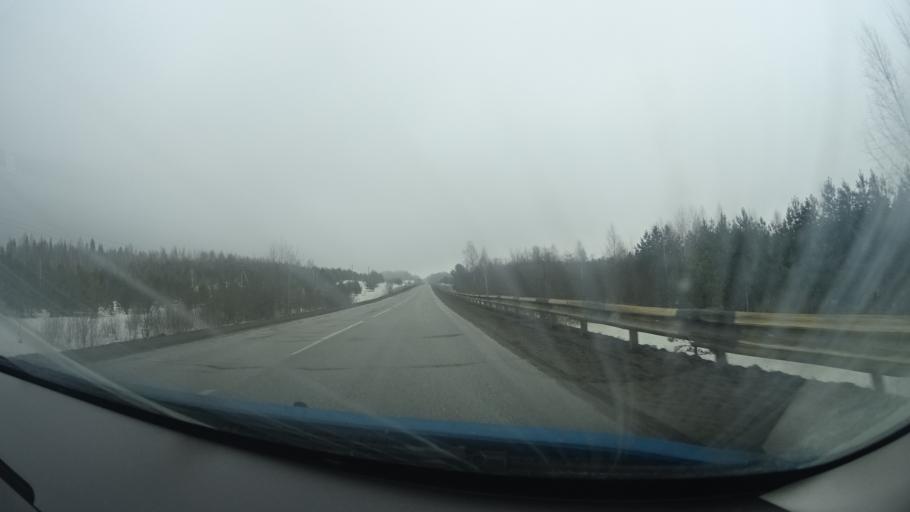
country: RU
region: Perm
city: Kuyeda
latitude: 56.4778
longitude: 55.7699
